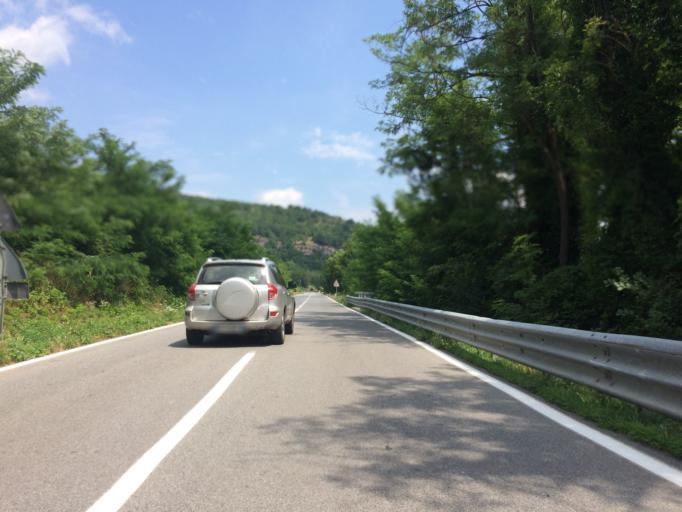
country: IT
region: Piedmont
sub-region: Provincia di Cuneo
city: Bagnasco
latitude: 44.2893
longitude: 8.0341
